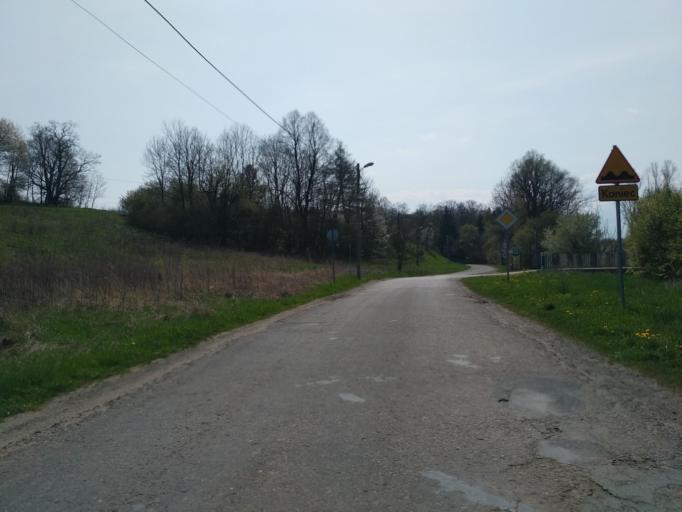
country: PL
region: Subcarpathian Voivodeship
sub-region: Powiat krosnienski
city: Miejsce Piastowe
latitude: 49.6336
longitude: 21.7310
